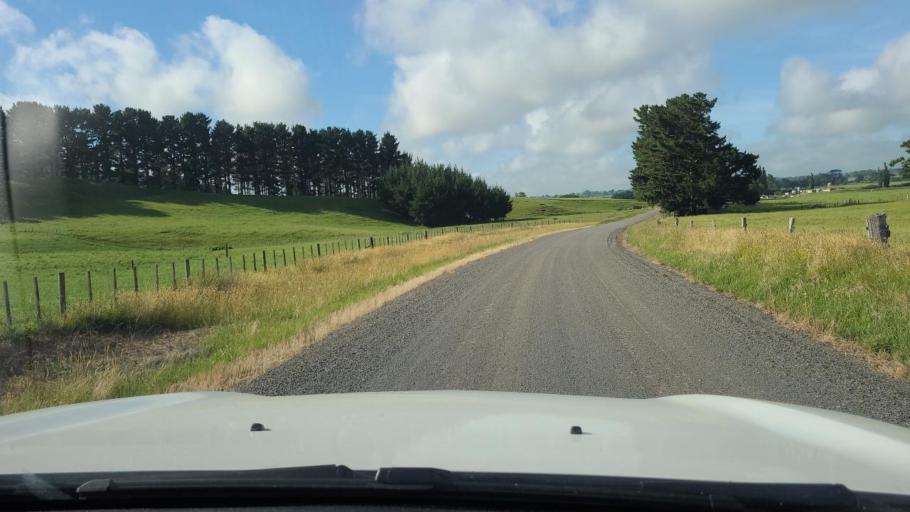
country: NZ
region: Bay of Plenty
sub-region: Western Bay of Plenty District
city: Katikati
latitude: -37.6074
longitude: 175.7972
